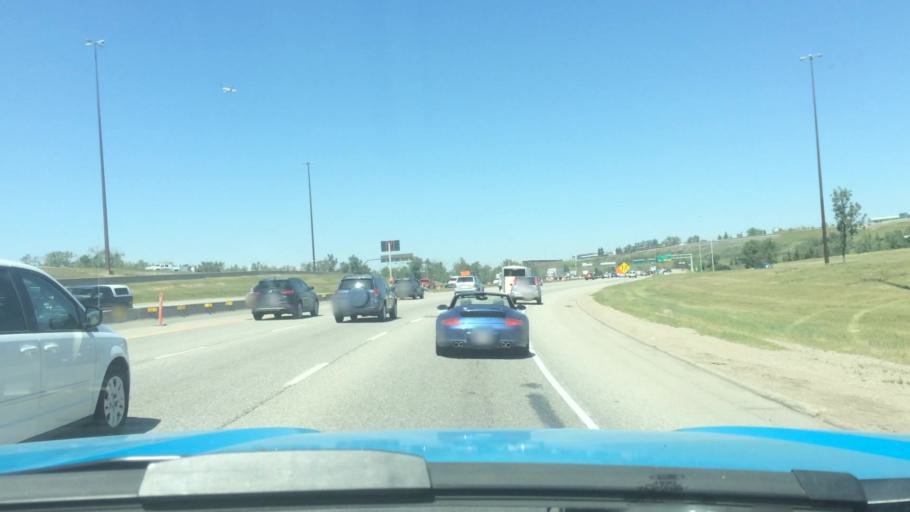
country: CA
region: Alberta
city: Calgary
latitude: 51.0375
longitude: -114.0052
